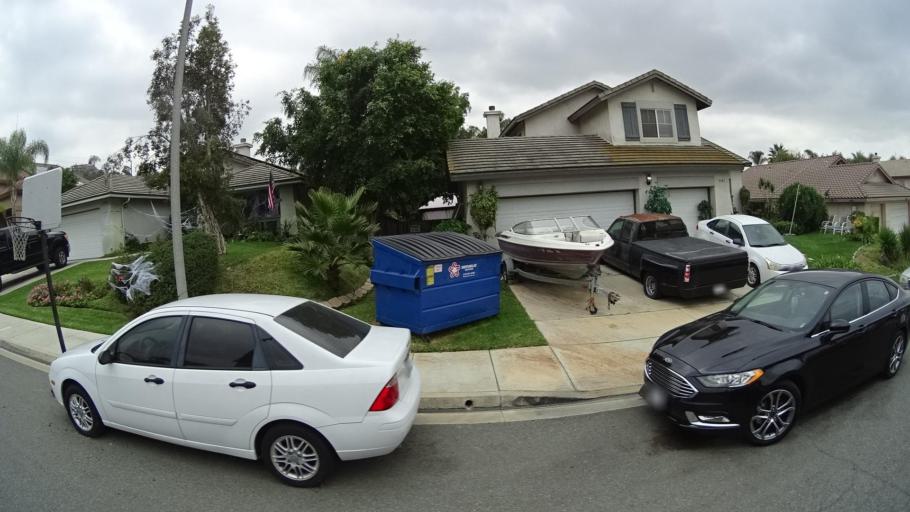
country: US
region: California
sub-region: San Diego County
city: Spring Valley
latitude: 32.7412
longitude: -116.9955
